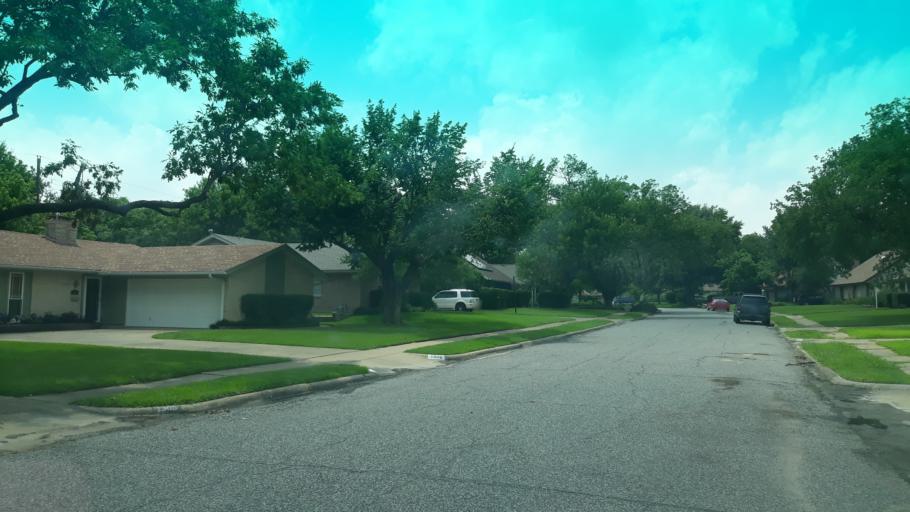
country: US
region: Texas
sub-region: Dallas County
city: Irving
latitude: 32.8543
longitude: -96.9626
